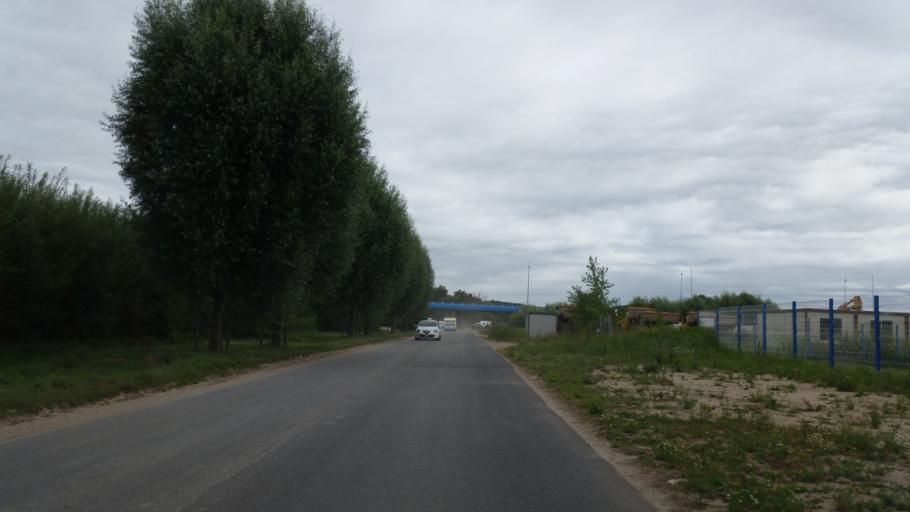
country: FR
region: Lower Normandy
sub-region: Departement du Calvados
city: La Riviere-Saint-Sauveur
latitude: 49.4193
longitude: 0.2726
